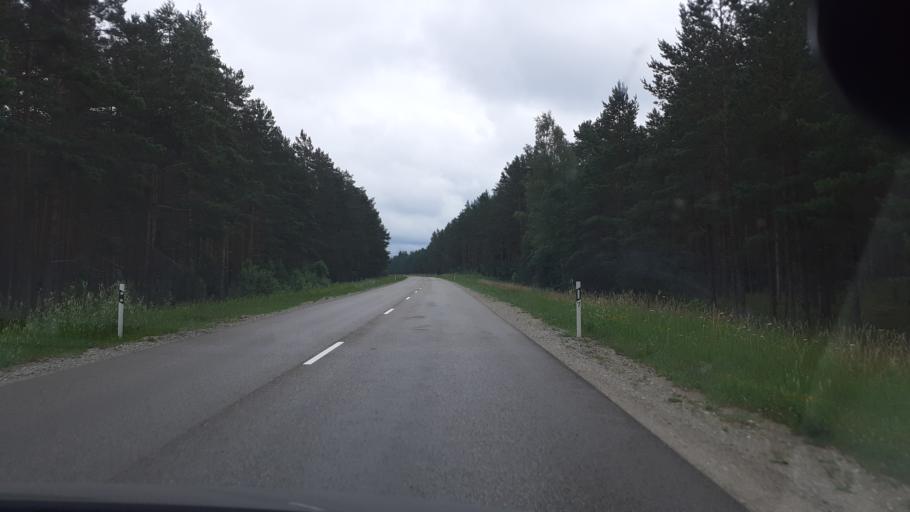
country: LV
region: Ventspils Rajons
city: Piltene
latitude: 57.1198
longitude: 21.7459
